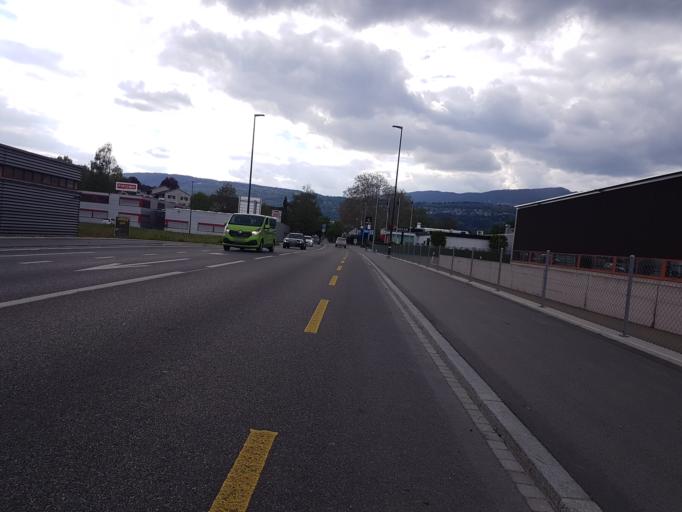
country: CH
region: Bern
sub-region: Biel/Bienne District
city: Brugg
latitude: 47.1423
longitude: 7.2855
